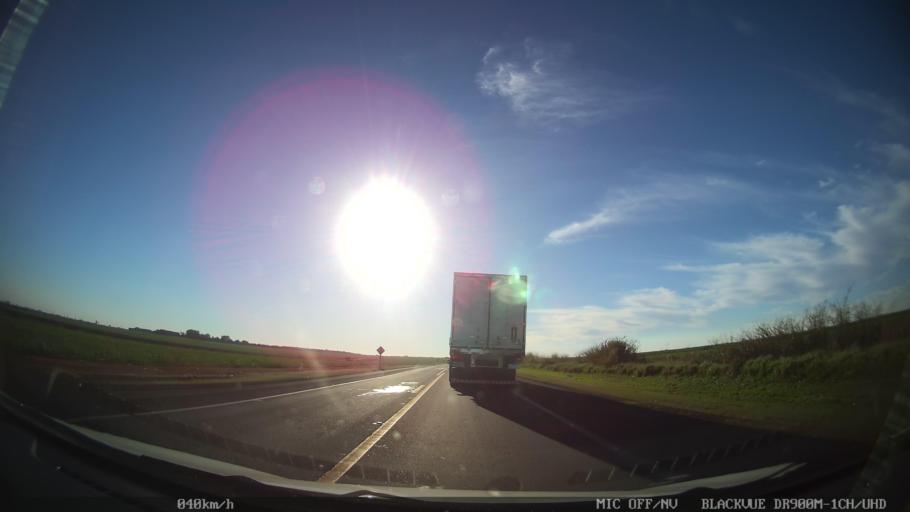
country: BR
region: Sao Paulo
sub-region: Americo Brasiliense
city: Americo Brasiliense
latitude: -21.7715
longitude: -48.1046
